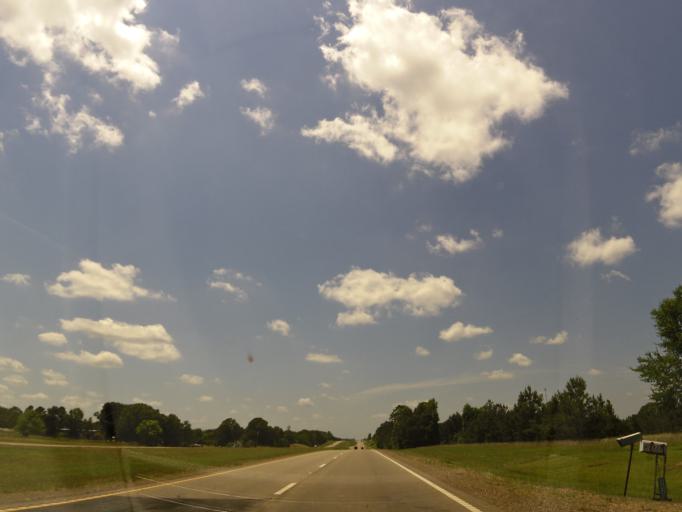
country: US
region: Mississippi
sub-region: Pontotoc County
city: Pontotoc
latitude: 34.2829
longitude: -89.1438
